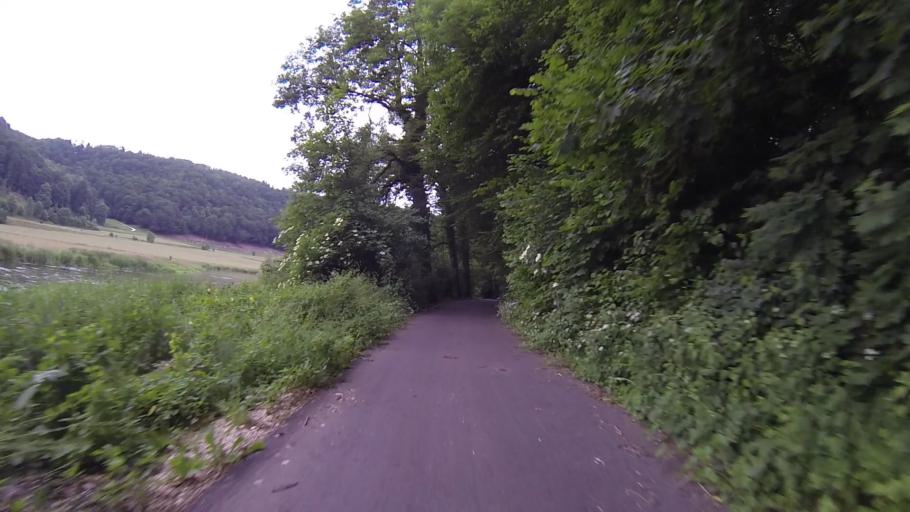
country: DE
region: Baden-Wuerttemberg
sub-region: Tuebingen Region
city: Blaubeuren
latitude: 48.4062
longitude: 9.8371
